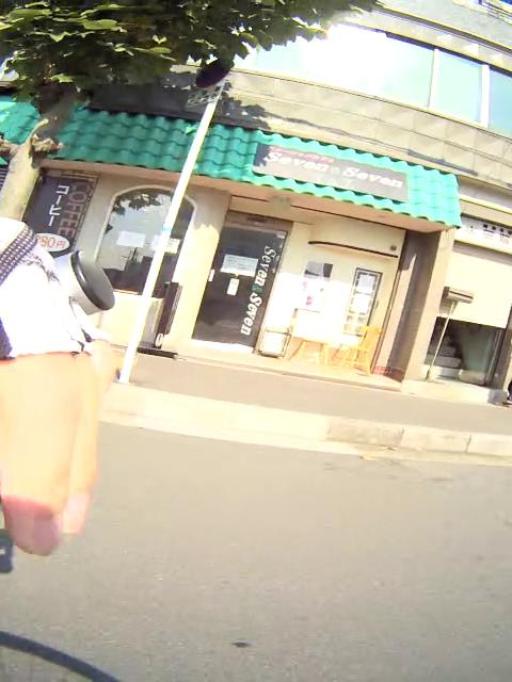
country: JP
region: Osaka
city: Suita
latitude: 34.7401
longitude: 135.5050
